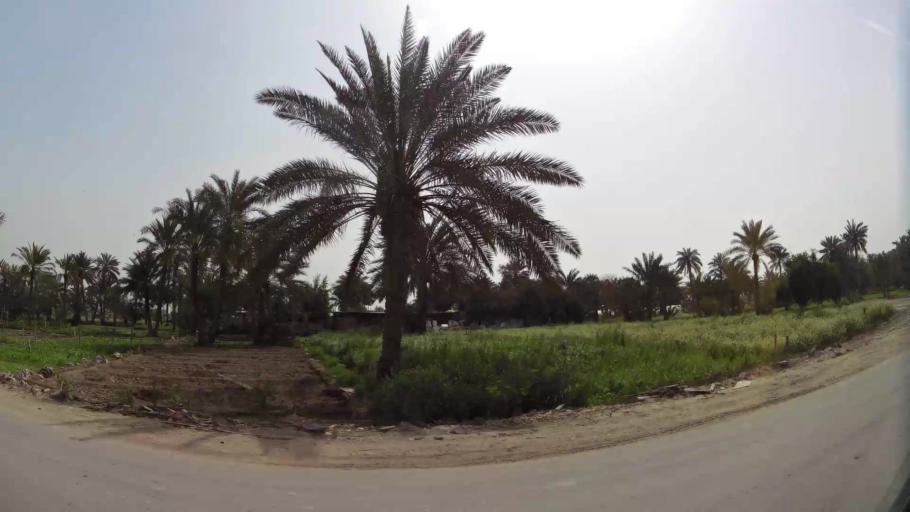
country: BH
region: Manama
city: Jidd Hafs
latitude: 26.2237
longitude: 50.5194
